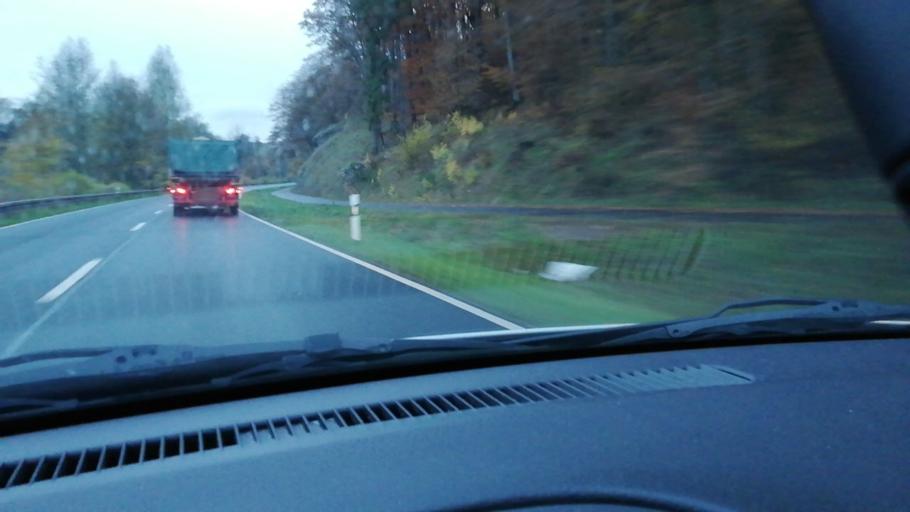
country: DE
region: Bavaria
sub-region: Regierungsbezirk Unterfranken
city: Hosbach
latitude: 50.0455
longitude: 9.1971
